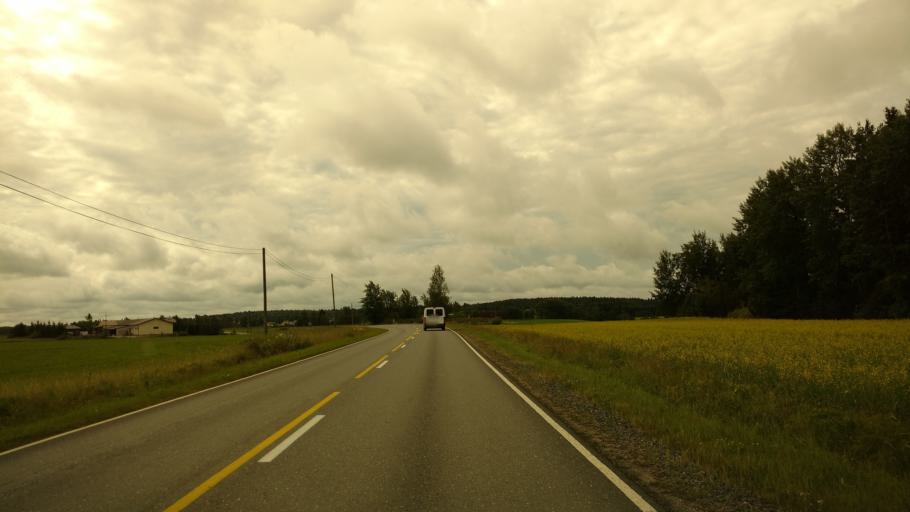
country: FI
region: Varsinais-Suomi
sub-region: Salo
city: Kuusjoki
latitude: 60.5456
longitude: 23.1625
